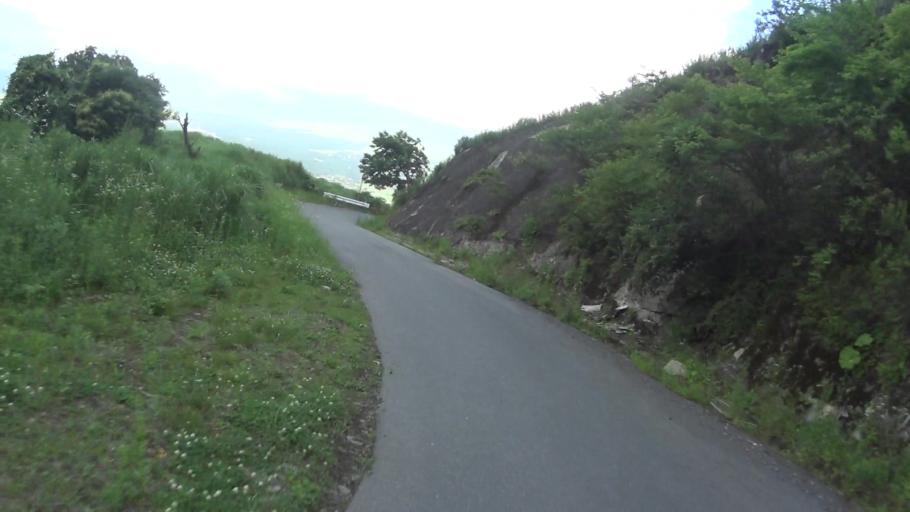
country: JP
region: Kumamoto
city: Aso
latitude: 32.9586
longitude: 130.9978
